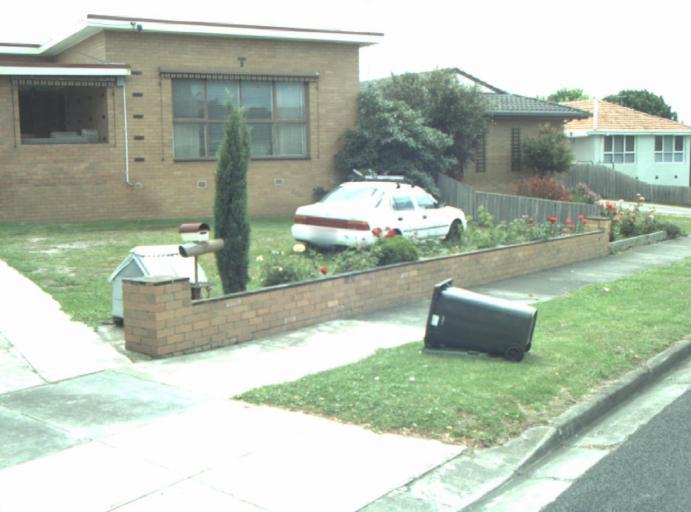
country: AU
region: Victoria
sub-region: Greater Geelong
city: Breakwater
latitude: -38.1862
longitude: 144.3353
